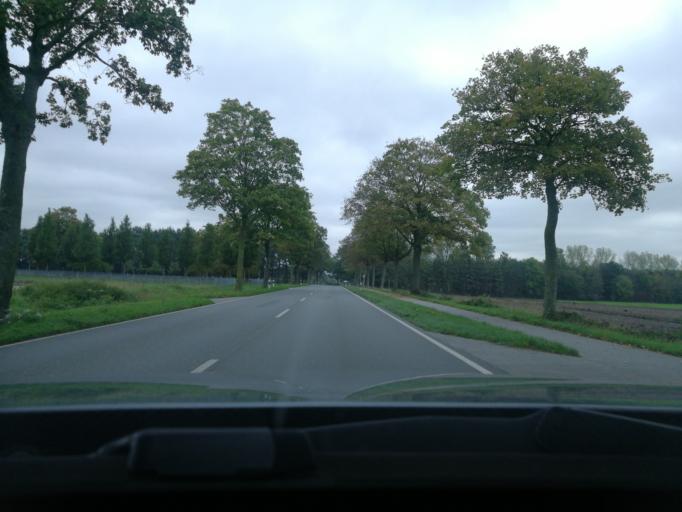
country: DE
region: North Rhine-Westphalia
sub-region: Regierungsbezirk Dusseldorf
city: Kevelaer
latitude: 51.5216
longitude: 6.2429
